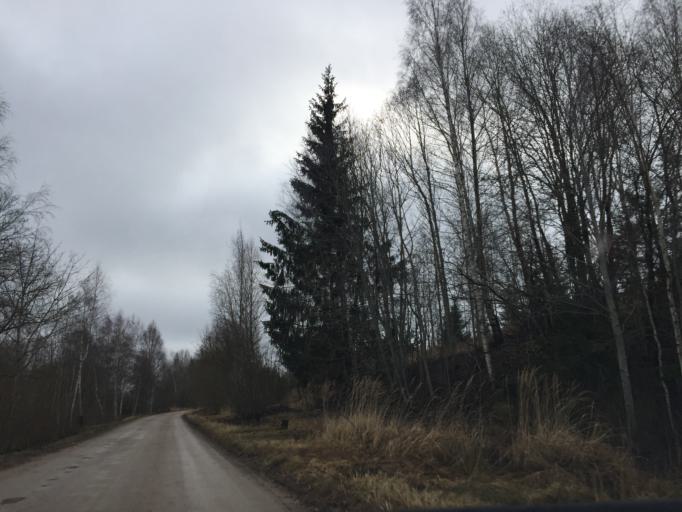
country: LV
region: Broceni
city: Broceni
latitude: 56.6606
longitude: 22.5542
